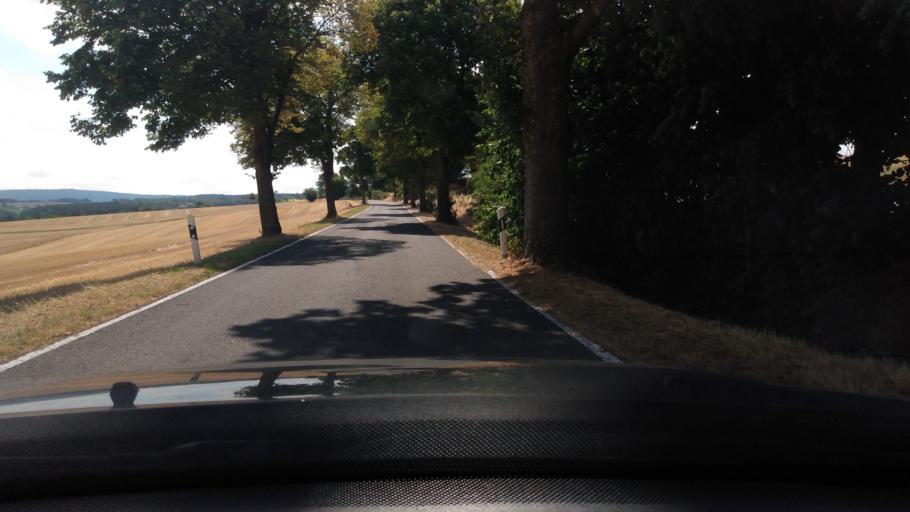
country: DE
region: Rheinland-Pfalz
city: Kleinich
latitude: 49.9016
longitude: 7.1731
